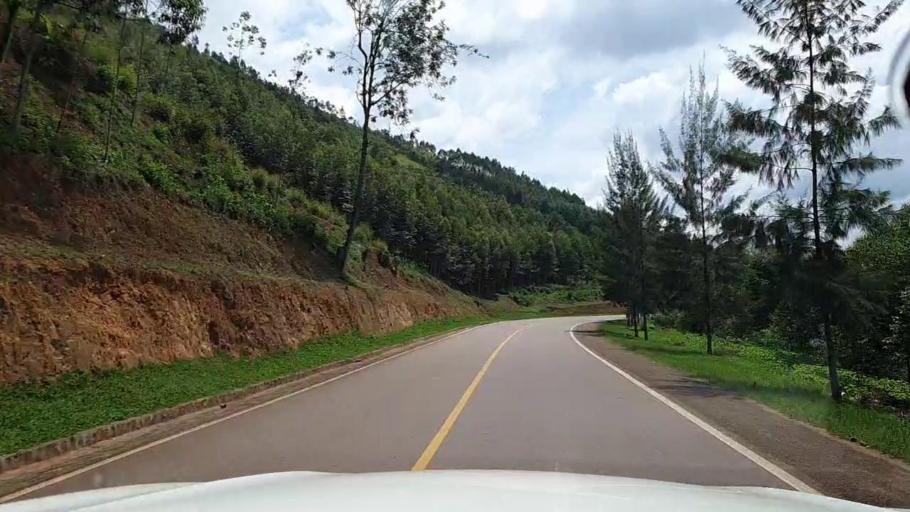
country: RW
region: Kigali
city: Kigali
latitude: -1.8126
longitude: 30.1031
